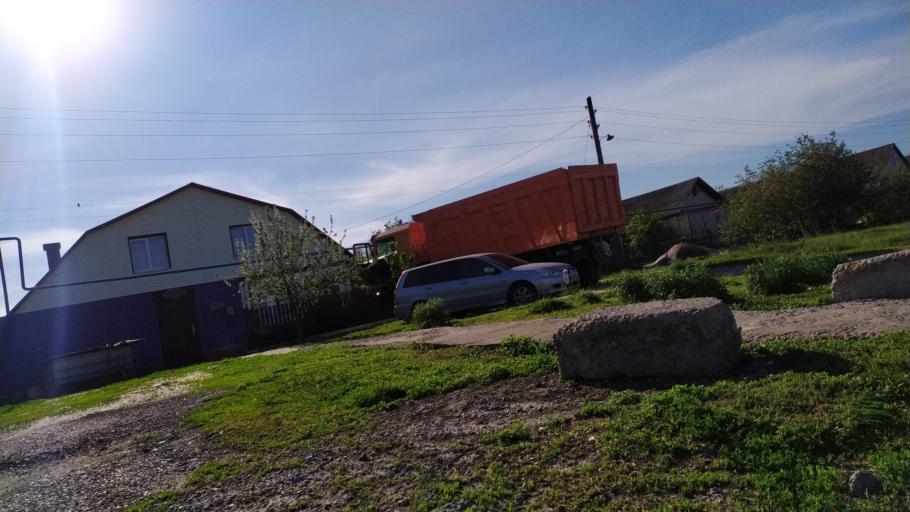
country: RU
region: Kursk
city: Kursk
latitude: 51.6356
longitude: 36.1494
